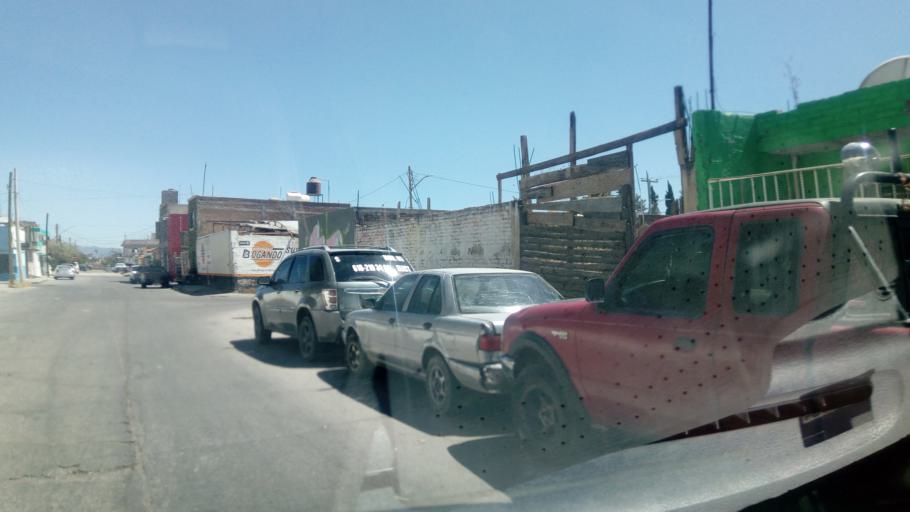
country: MX
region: Durango
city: Victoria de Durango
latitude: 24.0143
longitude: -104.6573
